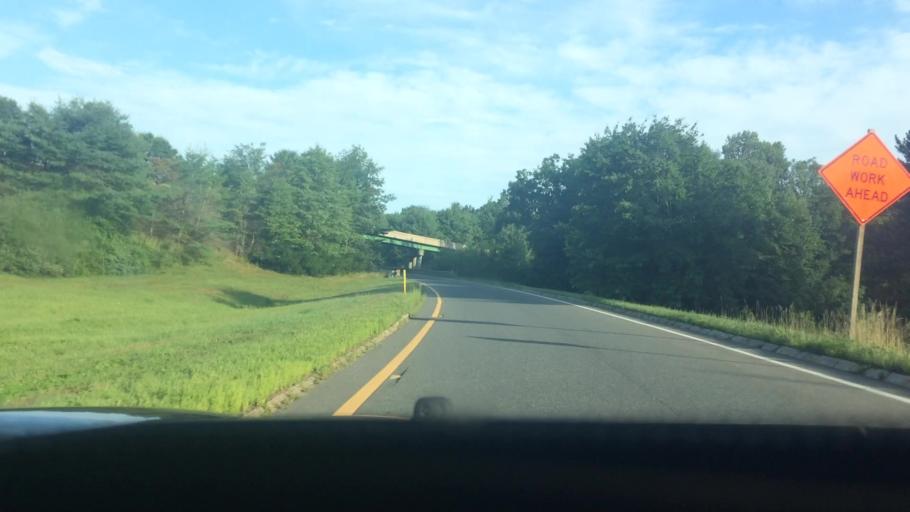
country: US
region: Massachusetts
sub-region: Franklin County
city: Greenfield
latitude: 42.6145
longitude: -72.5902
